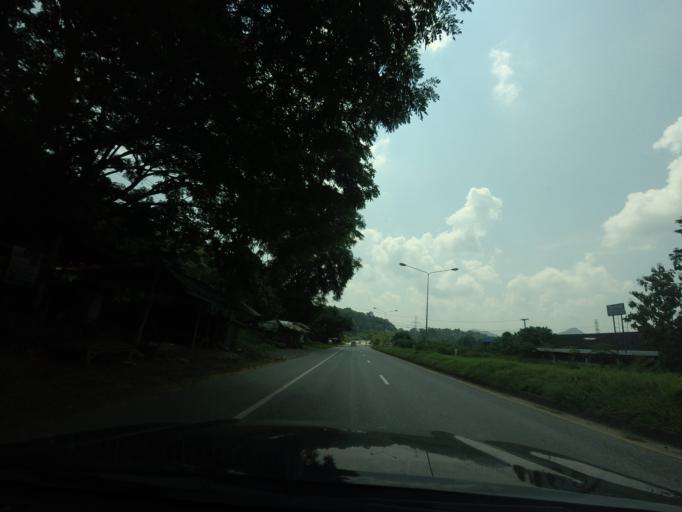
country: TH
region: Uttaradit
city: Lap Lae
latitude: 17.7889
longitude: 100.1176
